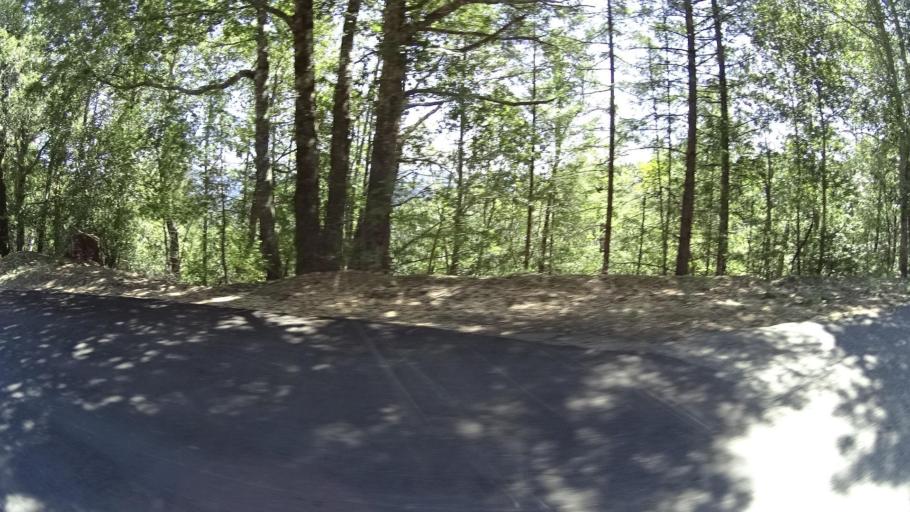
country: US
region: California
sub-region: Humboldt County
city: Redway
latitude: 40.1538
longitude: -124.0659
